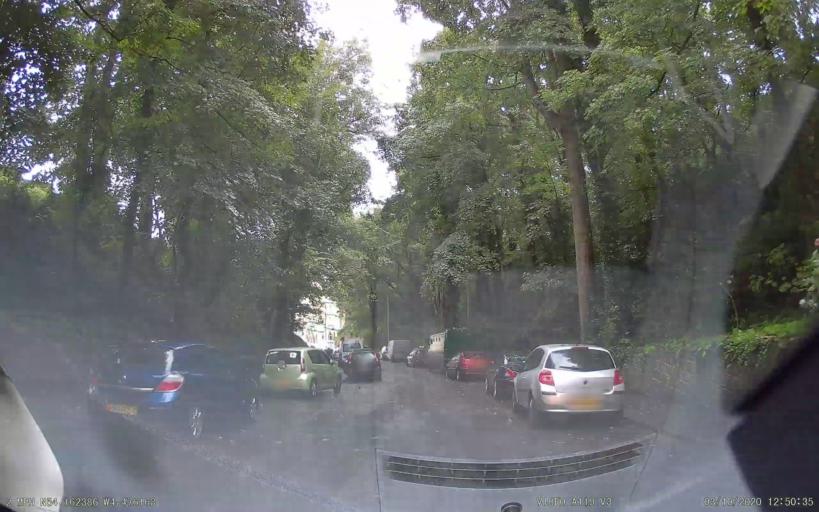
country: IM
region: Douglas
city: Douglas
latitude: 54.0000
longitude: -4.4762
